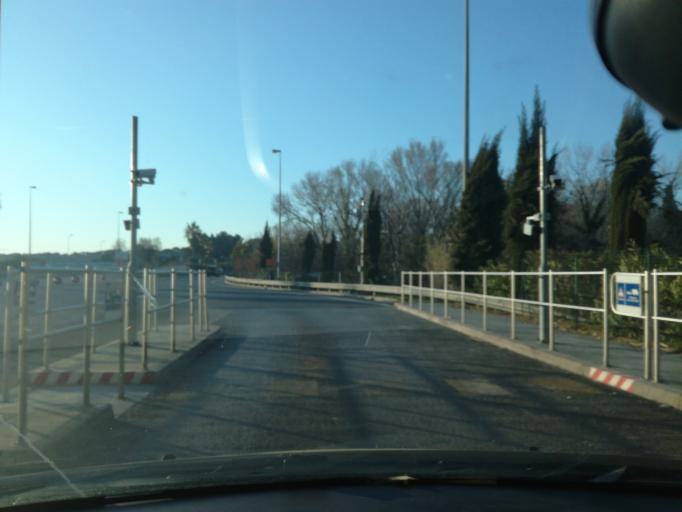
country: FR
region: Provence-Alpes-Cote d'Azur
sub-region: Departement du Var
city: Frejus
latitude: 43.4723
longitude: 6.7434
